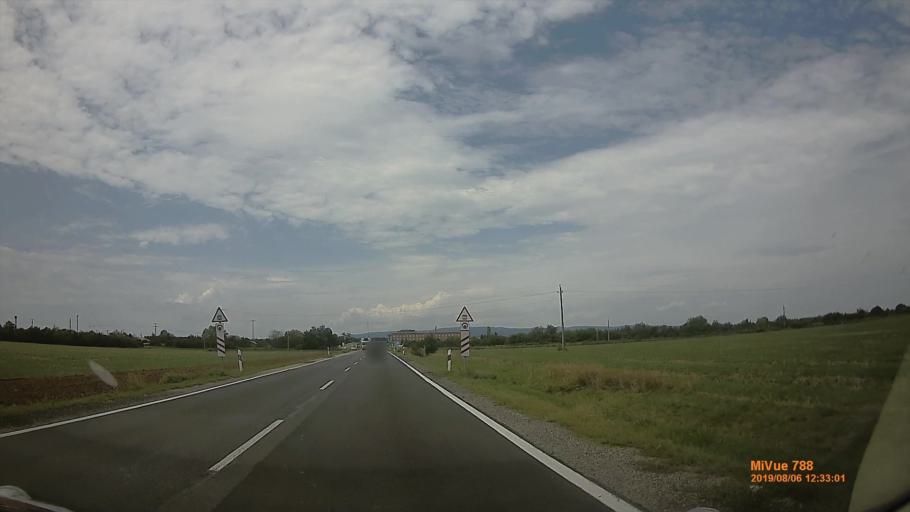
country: HU
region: Vas
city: Szombathely
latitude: 47.2518
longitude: 16.6381
